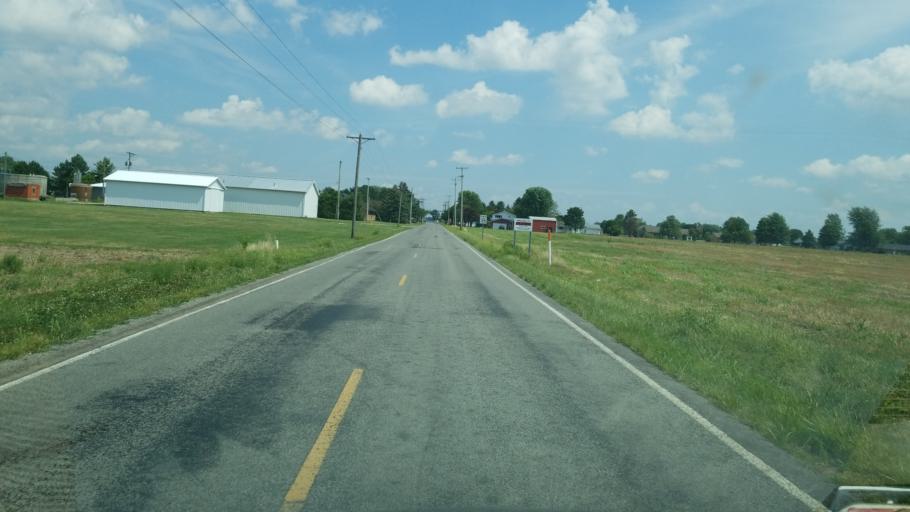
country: US
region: Ohio
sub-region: Hancock County
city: Arlington
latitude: 40.9067
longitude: -83.6565
